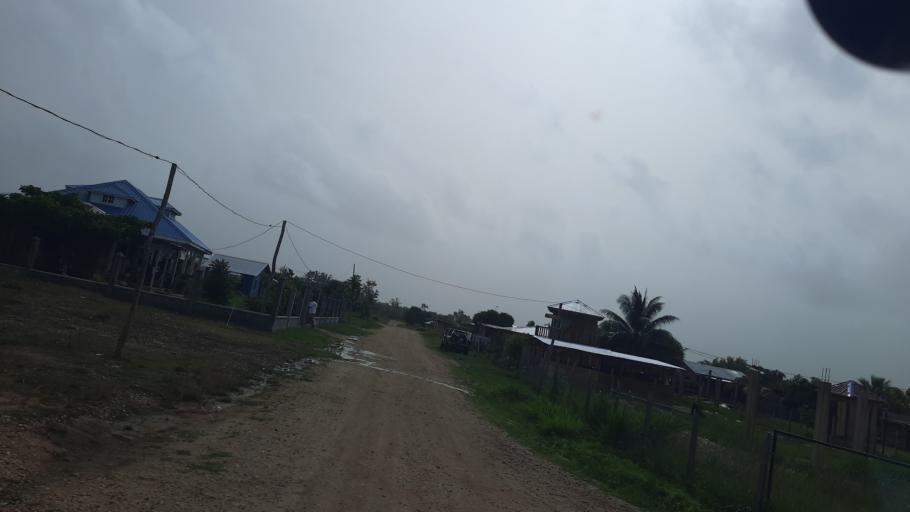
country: BZ
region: Cayo
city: Valley of Peace
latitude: 17.2530
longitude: -88.9391
